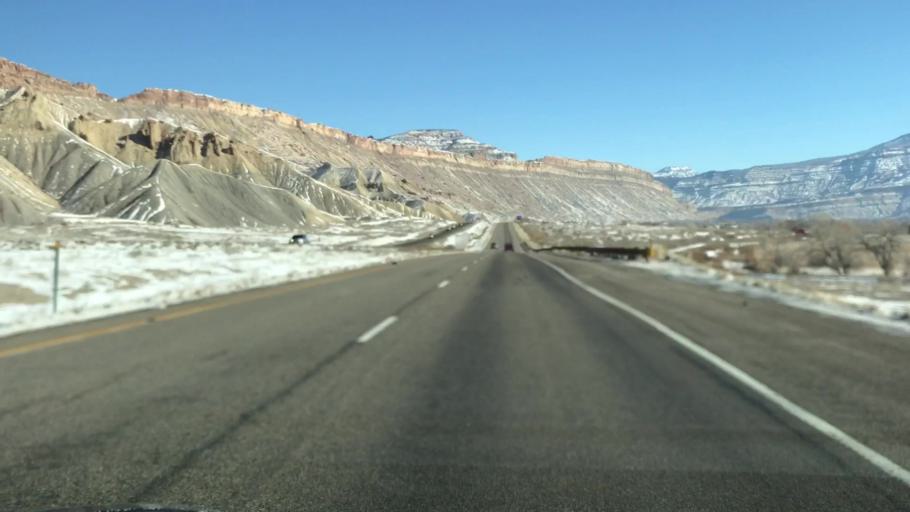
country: US
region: Colorado
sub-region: Mesa County
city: Clifton
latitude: 39.1131
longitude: -108.4073
